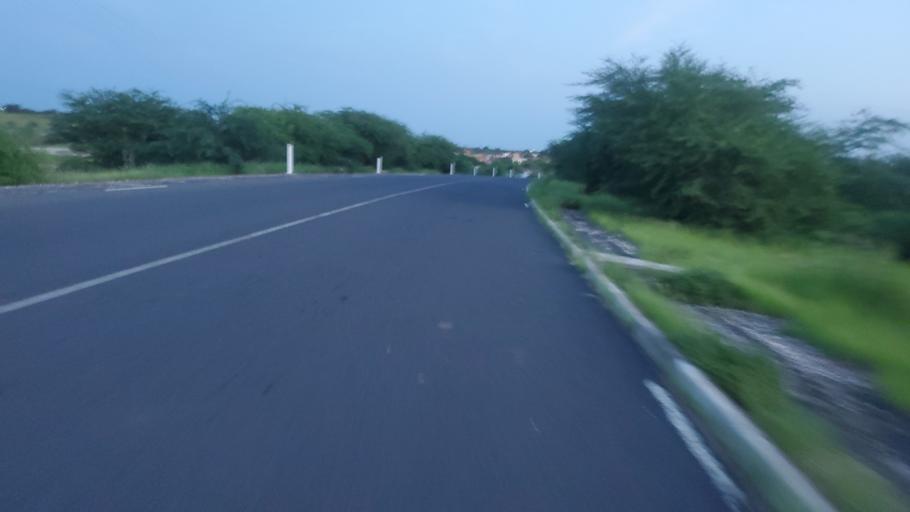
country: SN
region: Saint-Louis
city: Saint-Louis
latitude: 16.0750
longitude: -16.3892
